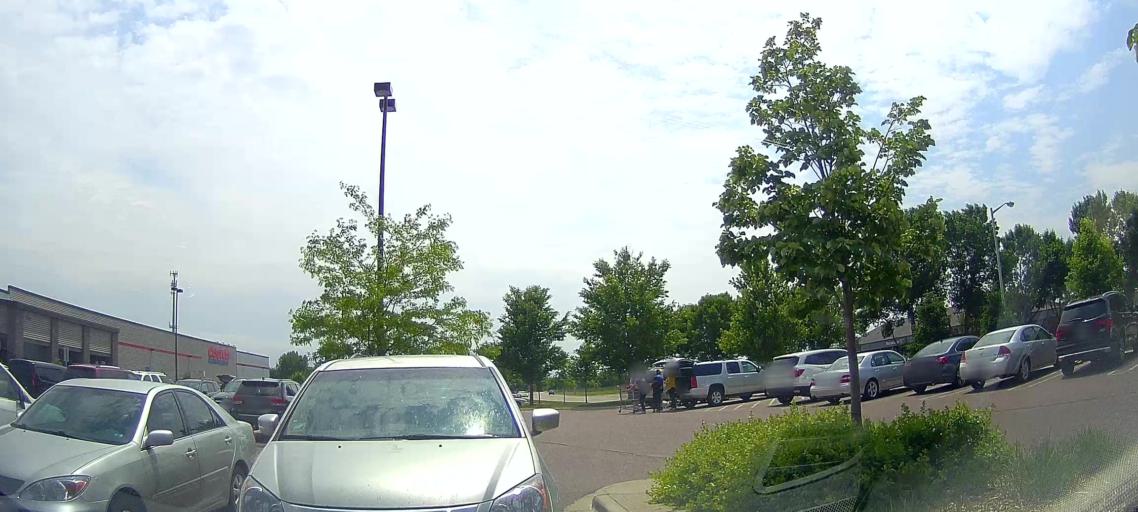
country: US
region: South Dakota
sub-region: Minnehaha County
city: Sioux Falls
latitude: 43.5131
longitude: -96.7407
